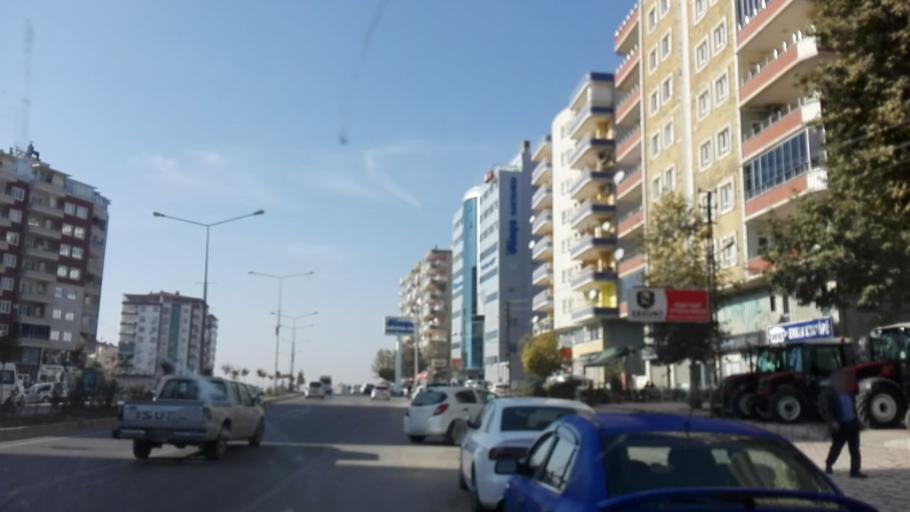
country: TR
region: Batman
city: Demiryol
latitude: 37.9016
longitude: 41.1441
